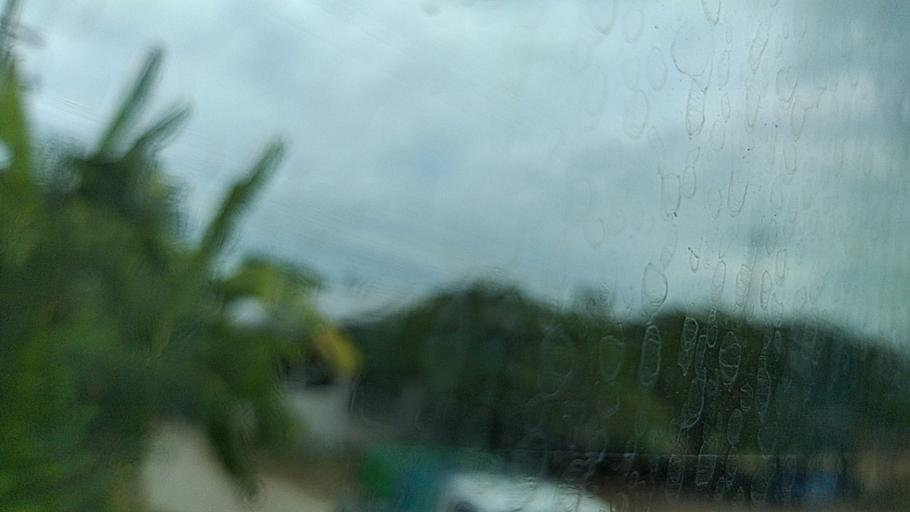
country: TH
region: Kalasin
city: Khong Chai
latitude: 16.1406
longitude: 103.4300
